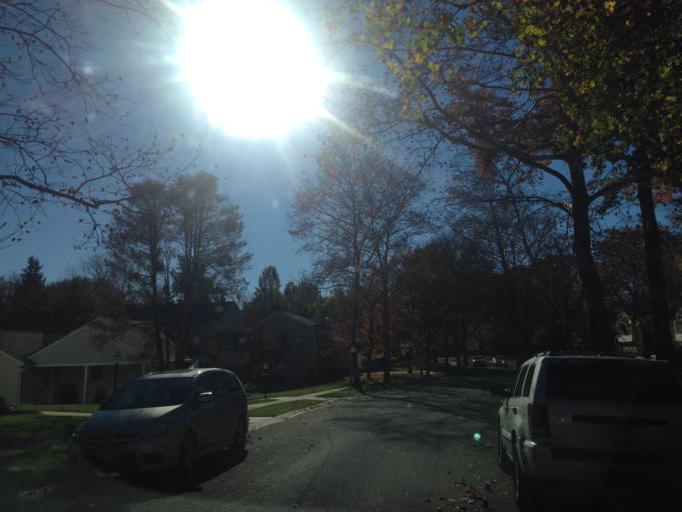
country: US
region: Maryland
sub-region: Howard County
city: Riverside
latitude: 39.2056
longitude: -76.8808
